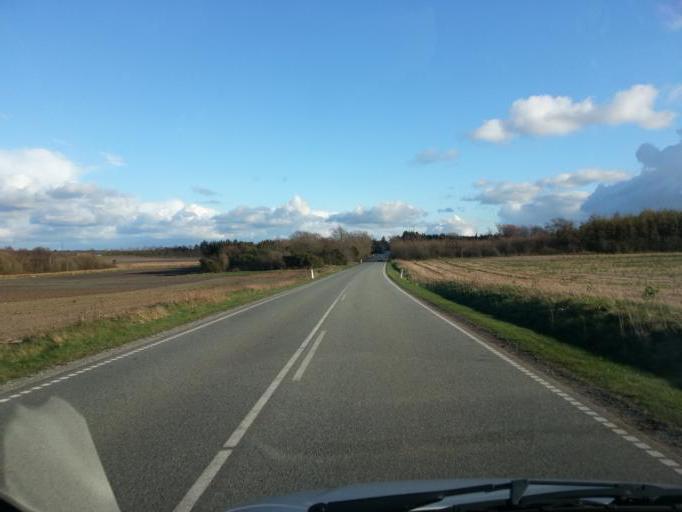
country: DK
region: Central Jutland
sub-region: Ringkobing-Skjern Kommune
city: Tarm
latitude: 55.8459
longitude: 8.5574
